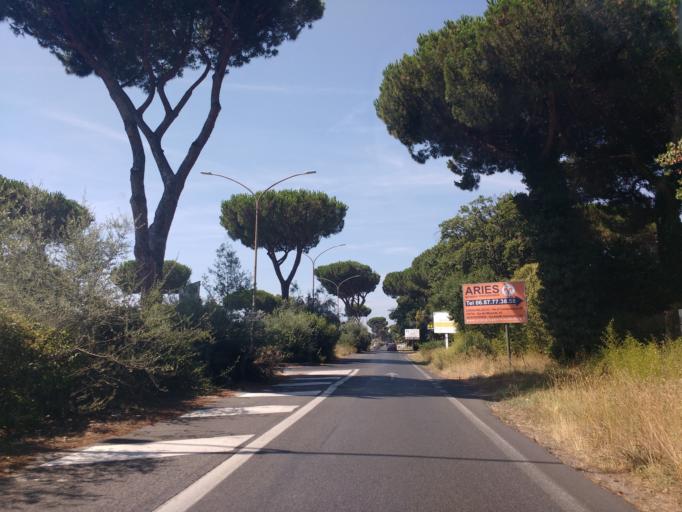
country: IT
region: Latium
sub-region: Citta metropolitana di Roma Capitale
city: Acilia-Castel Fusano-Ostia Antica
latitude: 41.7471
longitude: 12.3594
